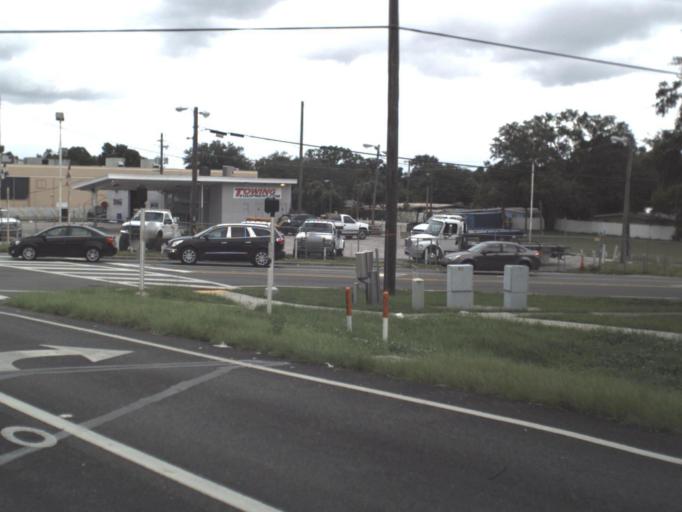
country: US
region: Florida
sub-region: Hillsborough County
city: East Lake-Orient Park
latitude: 27.9961
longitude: -82.3853
